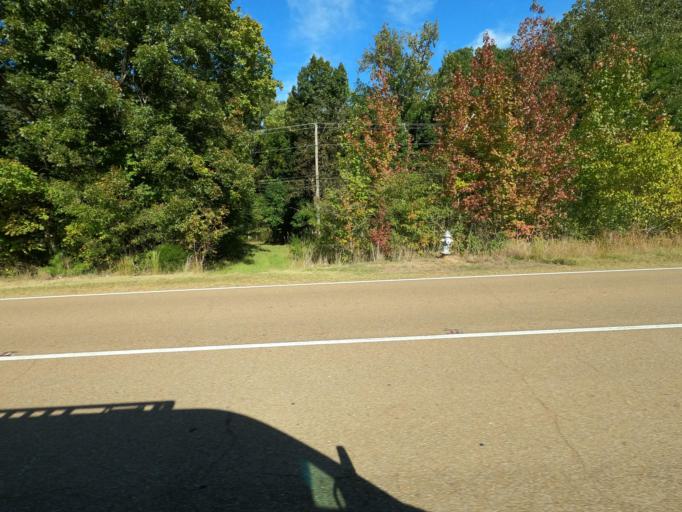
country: US
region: Tennessee
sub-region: Shelby County
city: Arlington
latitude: 35.2532
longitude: -89.6549
